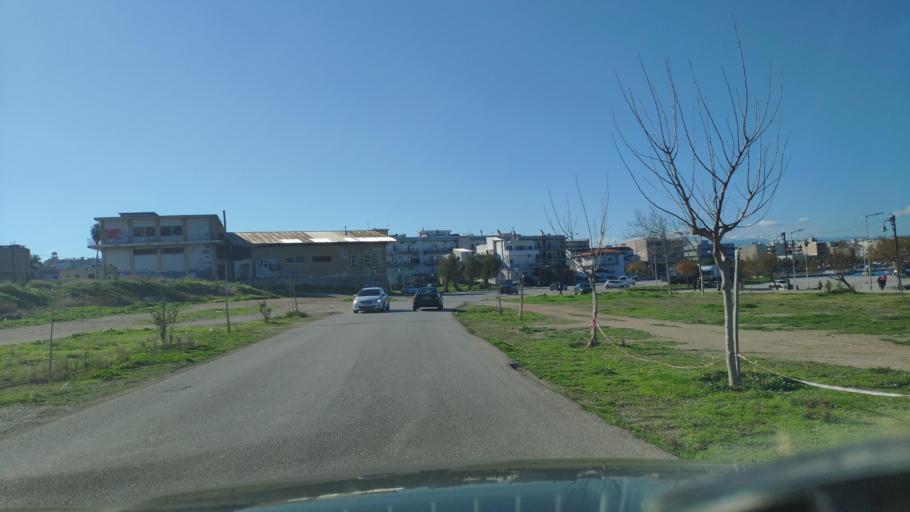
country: GR
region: Peloponnese
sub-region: Nomos Korinthias
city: Korinthos
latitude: 37.9401
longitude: 22.9409
